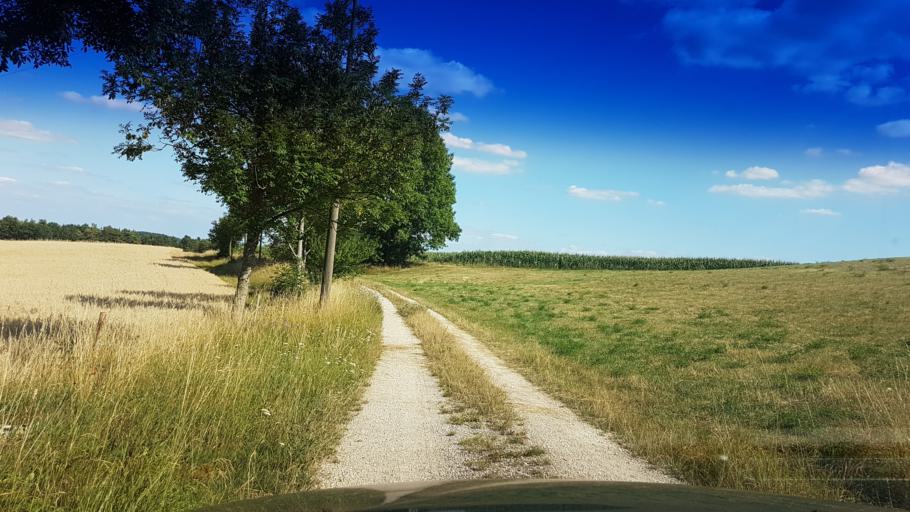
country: DE
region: Bavaria
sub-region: Upper Franconia
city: Poxdorf
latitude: 49.8941
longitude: 11.0897
